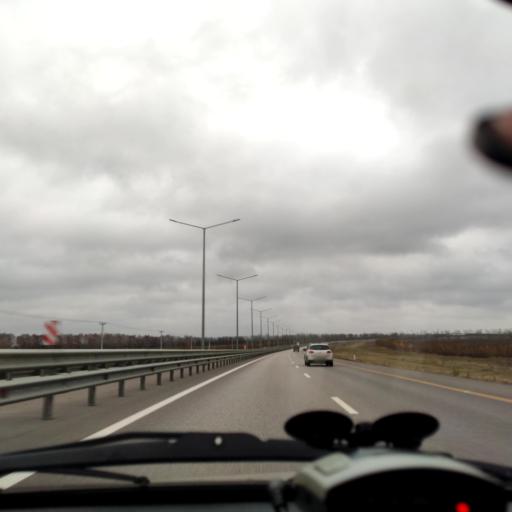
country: RU
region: Voronezj
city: Podkletnoye
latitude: 51.5853
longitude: 39.4514
